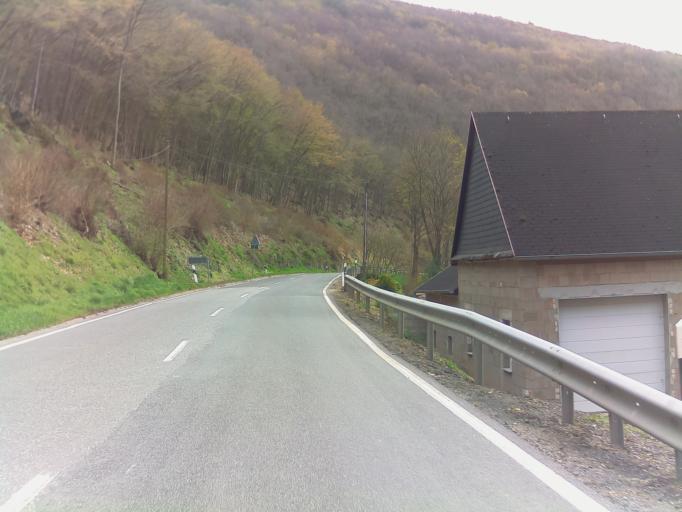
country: DE
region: Rheinland-Pfalz
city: Bruschied
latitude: 49.8272
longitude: 7.3975
